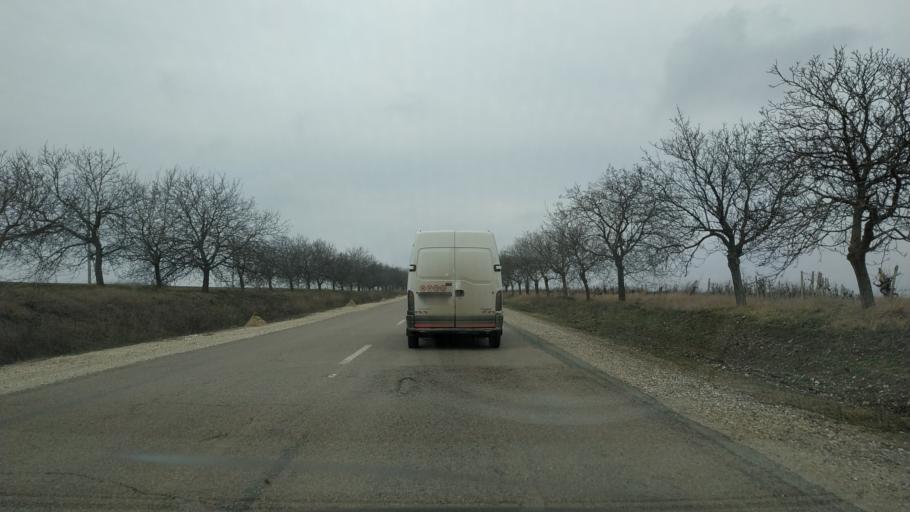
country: MD
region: Cahul
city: Cahul
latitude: 45.9564
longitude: 28.3939
